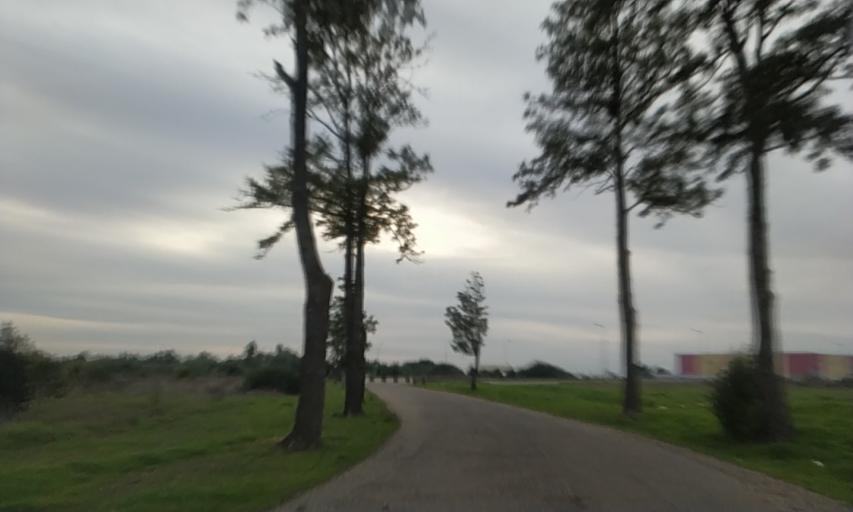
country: PT
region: Setubal
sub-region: Setubal
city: Setubal
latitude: 38.4977
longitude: -8.8225
